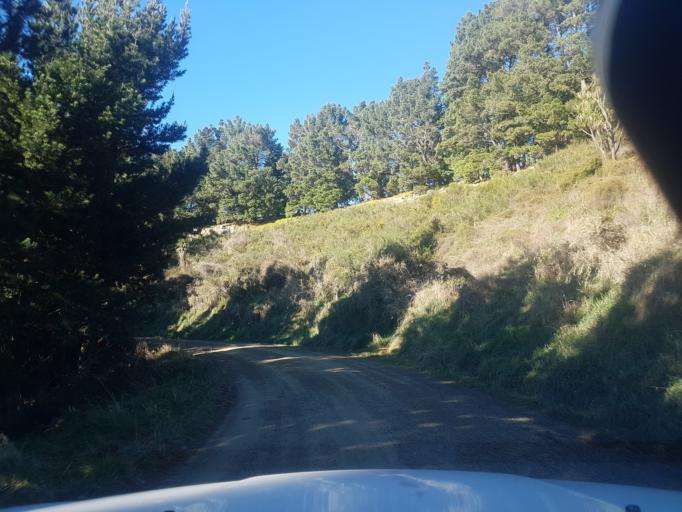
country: NZ
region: Canterbury
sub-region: Timaru District
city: Pleasant Point
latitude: -44.3452
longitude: 171.0751
